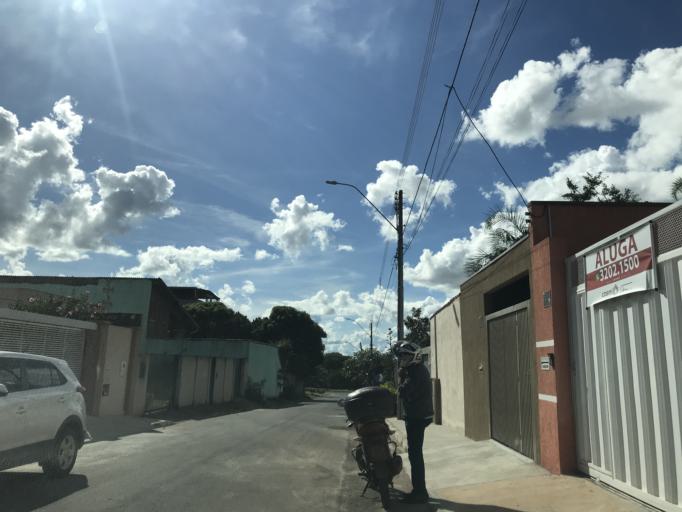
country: BR
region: Federal District
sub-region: Brasilia
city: Brasilia
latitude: -15.7368
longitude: -47.7505
